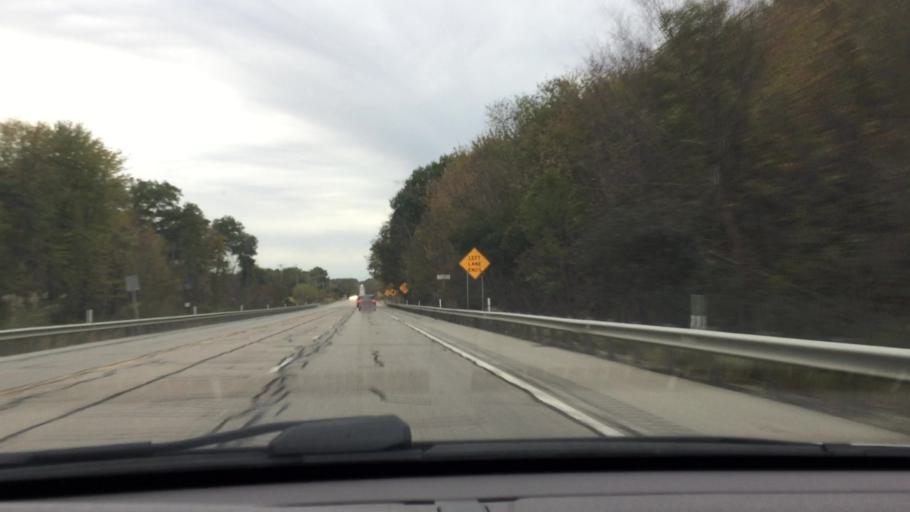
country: US
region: Ohio
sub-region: Mahoning County
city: Lowellville
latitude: 41.0652
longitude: -80.4616
